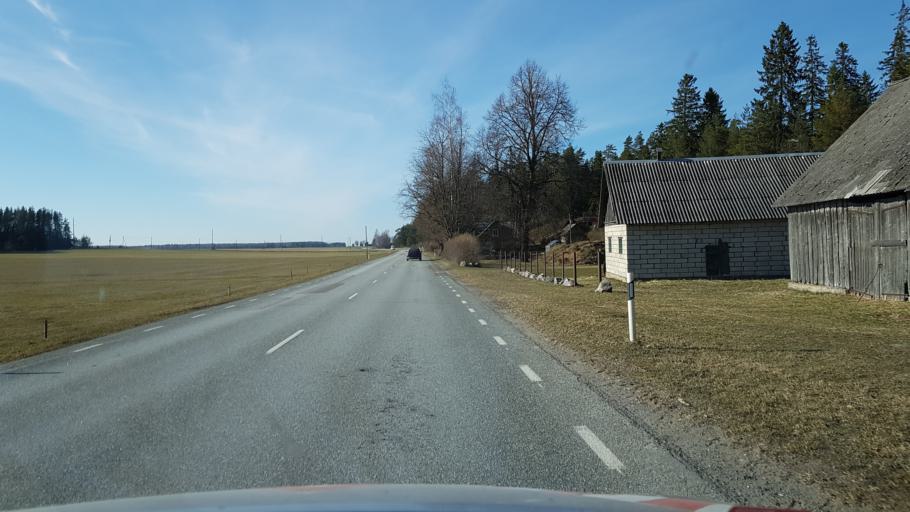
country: EE
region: Laeaene-Virumaa
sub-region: Vinni vald
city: Vinni
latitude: 59.1895
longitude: 26.5728
